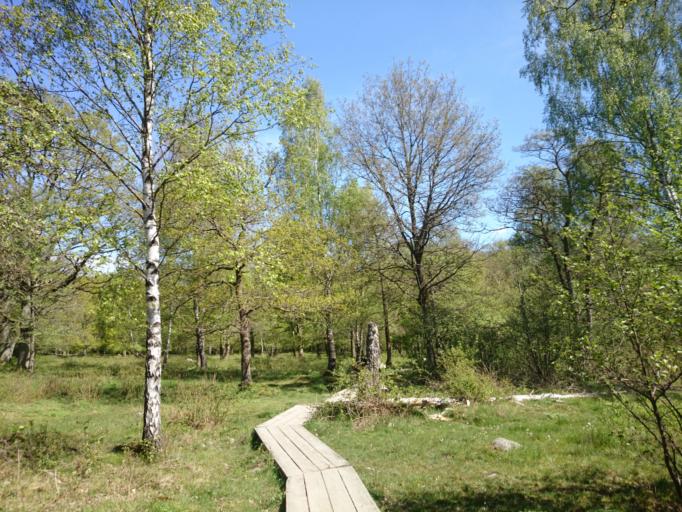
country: SE
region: Skane
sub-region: Lunds Kommun
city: Genarp
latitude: 55.6852
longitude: 13.4024
